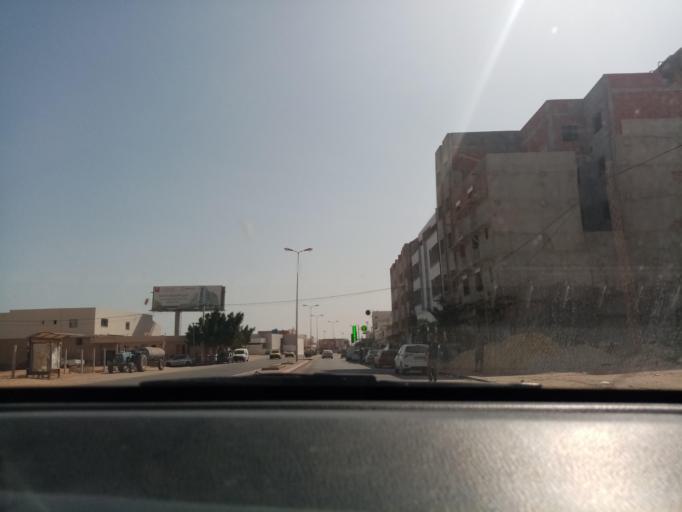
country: TN
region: Qabis
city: Gabes
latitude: 33.8504
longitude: 10.1106
